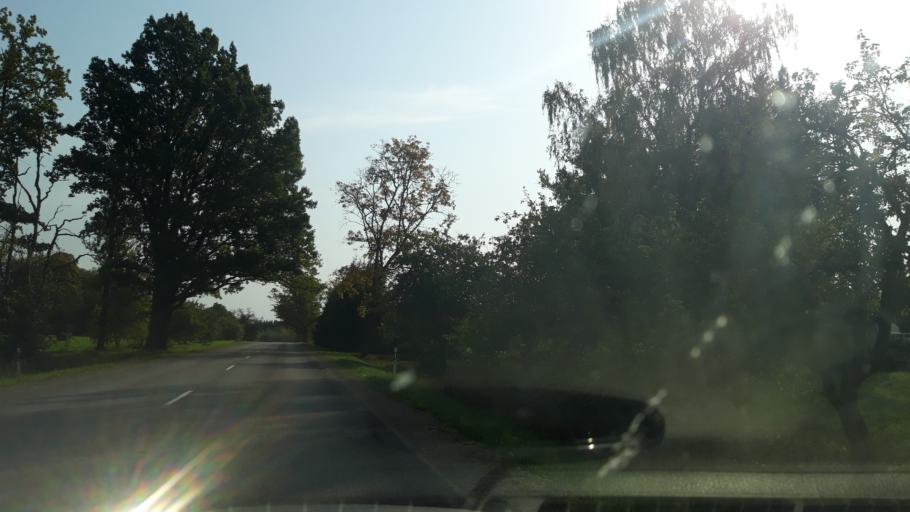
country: LV
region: Koceni
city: Koceni
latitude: 57.6268
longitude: 25.2677
